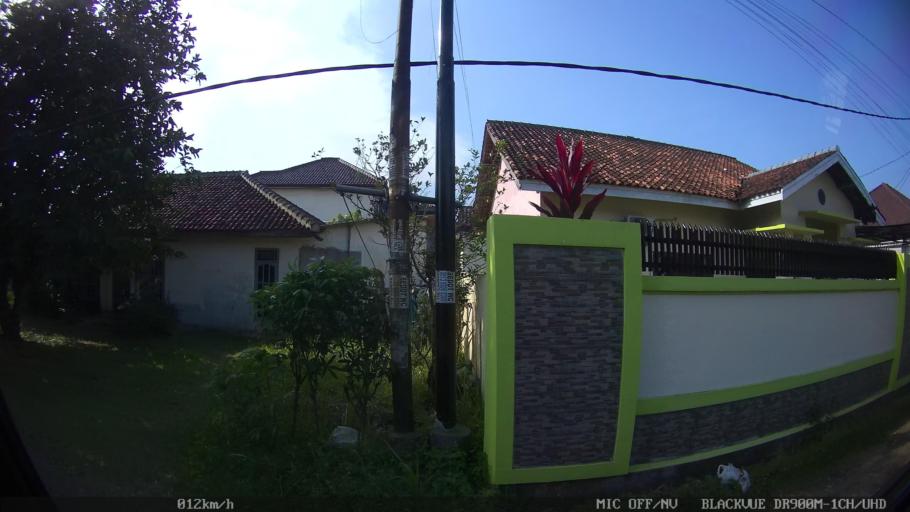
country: ID
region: Lampung
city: Kedaton
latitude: -5.3791
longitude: 105.2337
